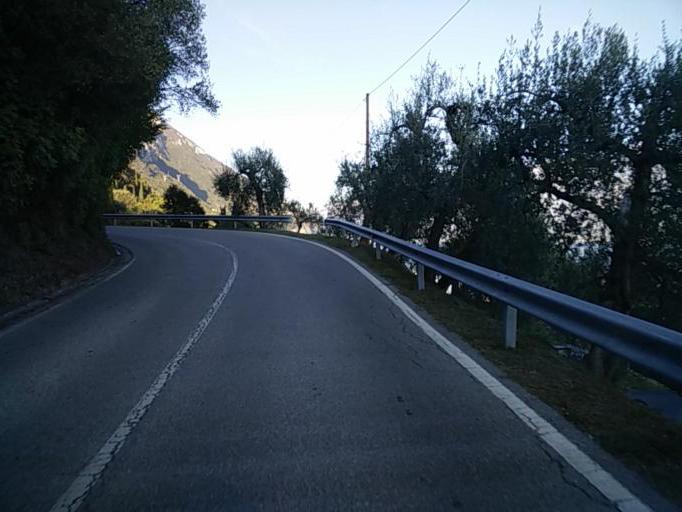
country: IT
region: Lombardy
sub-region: Provincia di Brescia
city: Gargnano
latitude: 45.6815
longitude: 10.6492
